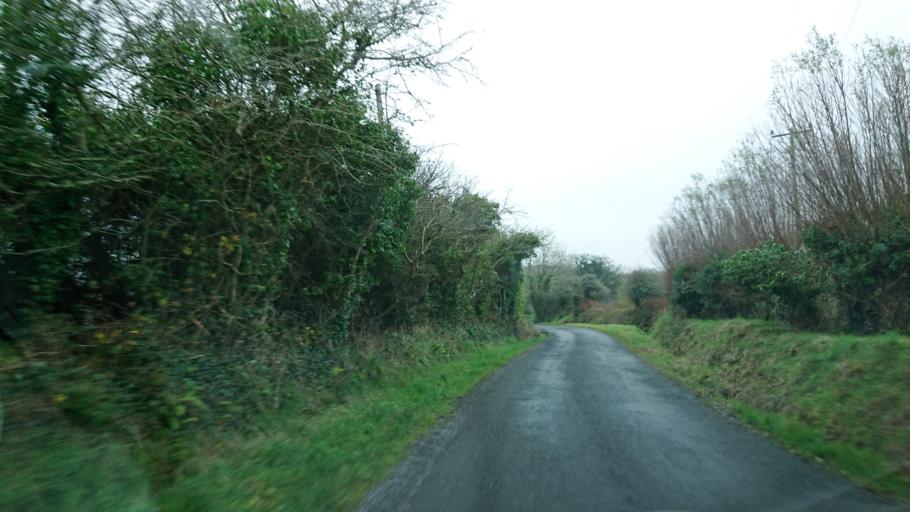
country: IE
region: Munster
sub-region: Waterford
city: Dunmore East
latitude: 52.1756
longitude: -7.0162
